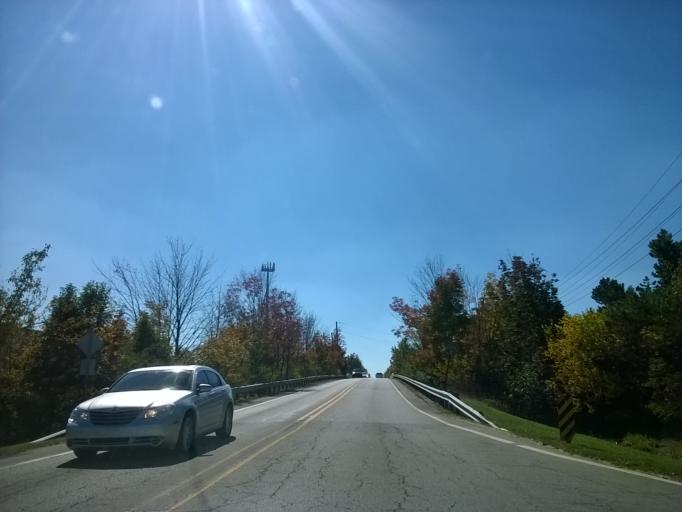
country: US
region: Indiana
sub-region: Marion County
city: Meridian Hills
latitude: 39.9262
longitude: -86.1841
